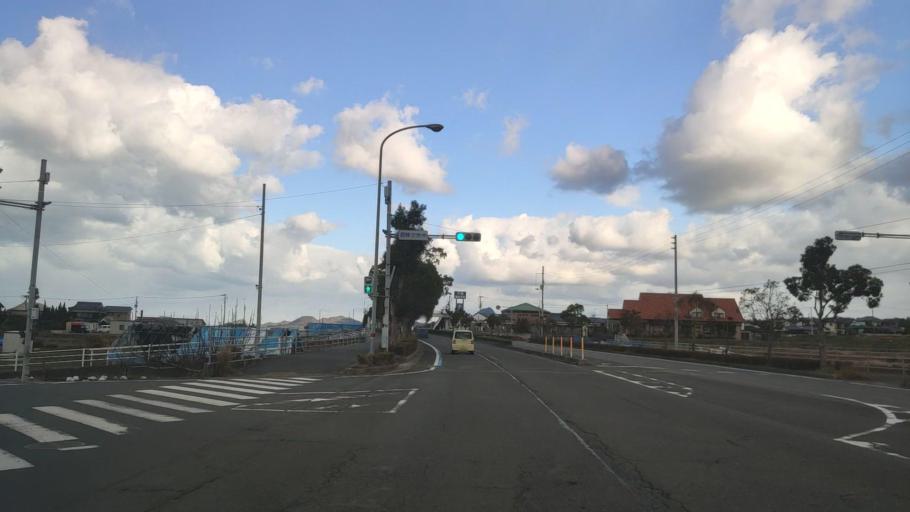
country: JP
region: Ehime
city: Hojo
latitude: 33.9379
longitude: 132.7732
